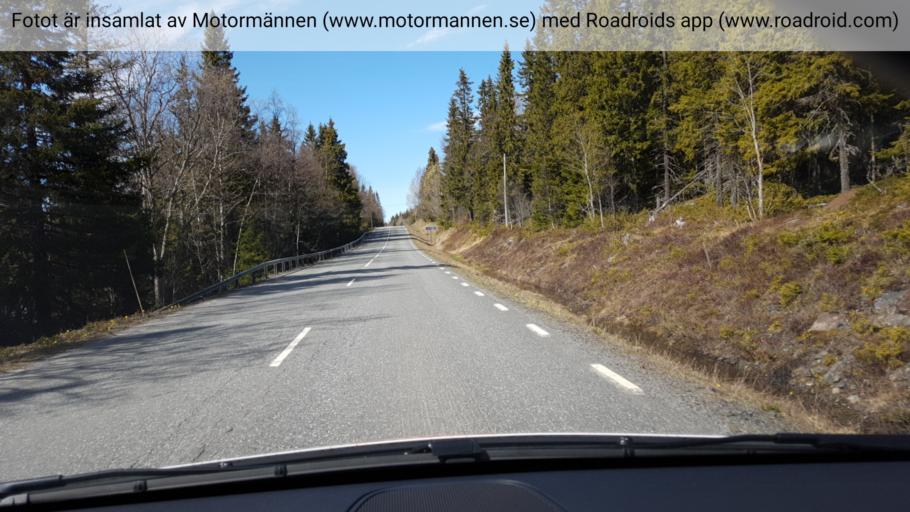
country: SE
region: Jaemtland
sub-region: Are Kommun
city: Are
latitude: 63.4976
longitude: 13.1714
